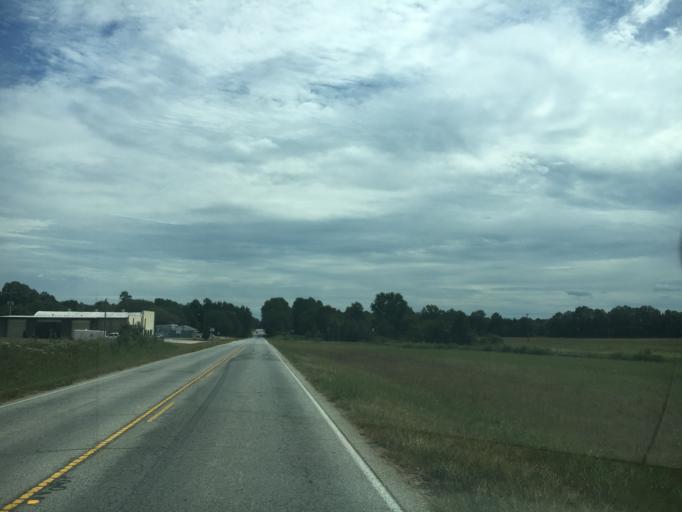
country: US
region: South Carolina
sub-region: Laurens County
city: Laurens
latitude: 34.5488
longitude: -82.0722
